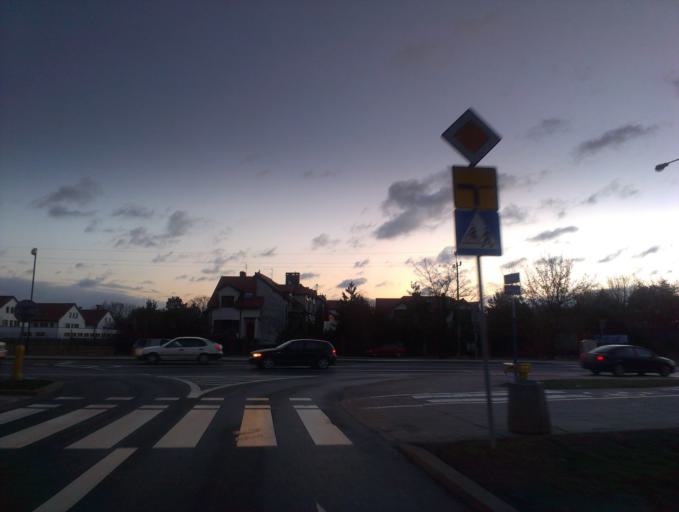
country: PL
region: Masovian Voivodeship
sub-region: Warszawa
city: Kabaty
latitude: 52.1330
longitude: 21.0751
